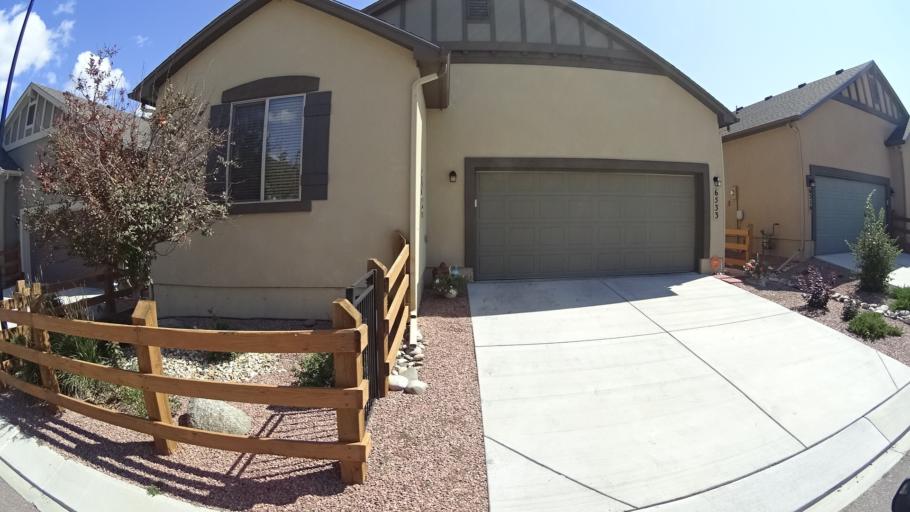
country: US
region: Colorado
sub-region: El Paso County
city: Cimarron Hills
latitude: 38.9273
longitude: -104.6881
